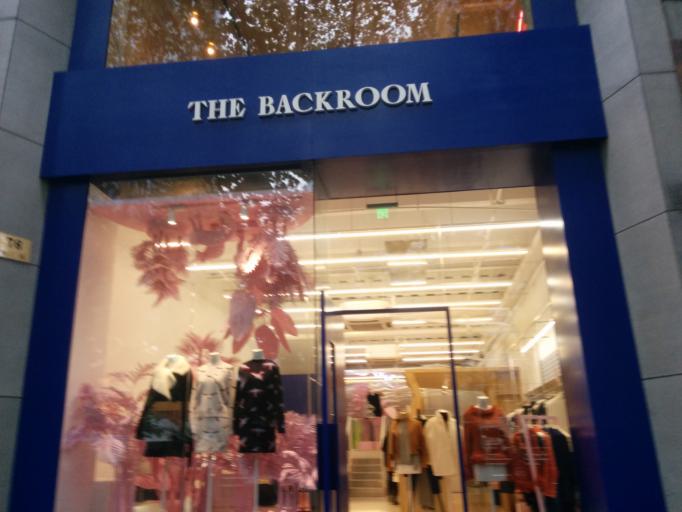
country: CN
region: Shanghai Shi
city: Shanghai
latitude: 31.2255
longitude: 121.4464
